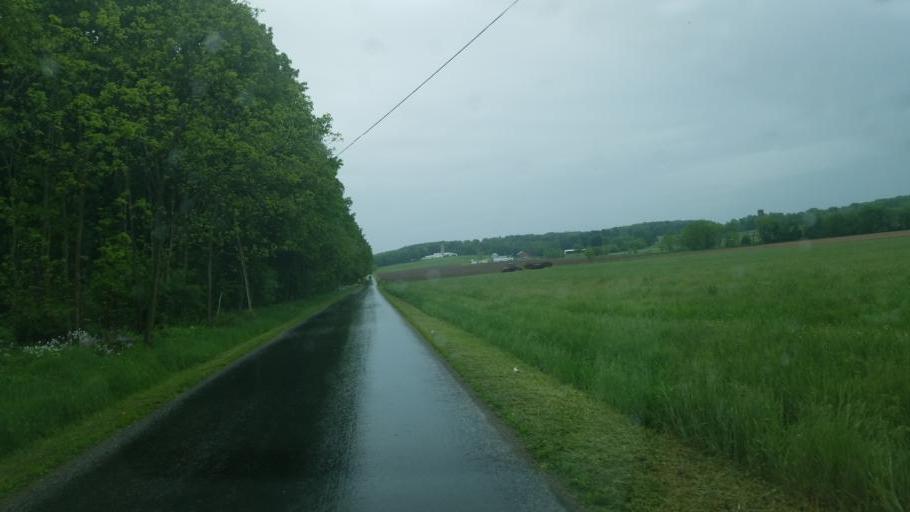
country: US
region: Ohio
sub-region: Wayne County
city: Apple Creek
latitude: 40.7585
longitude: -81.8536
